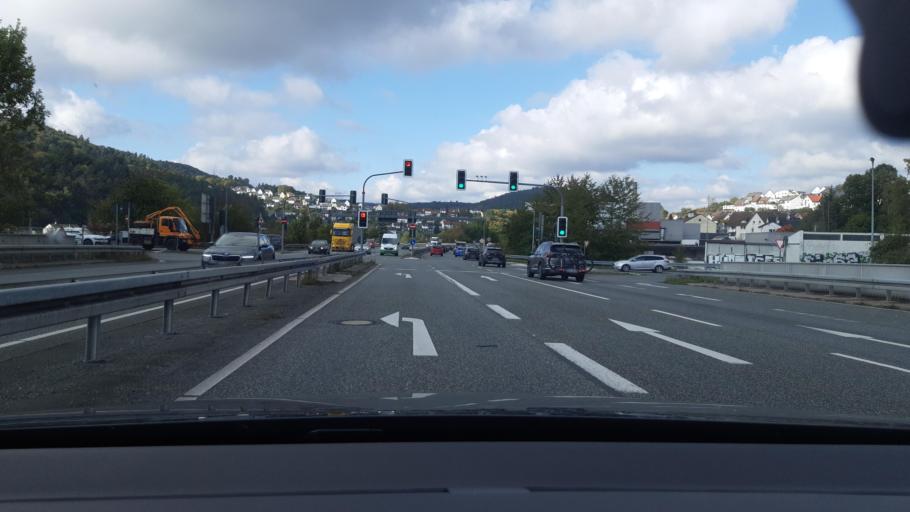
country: DE
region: Hesse
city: Herborn
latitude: 50.6871
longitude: 8.3092
